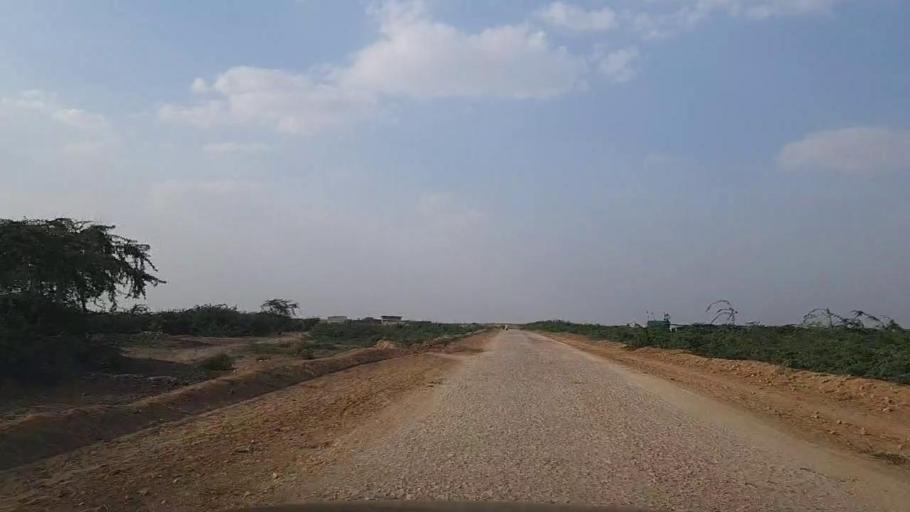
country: PK
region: Sindh
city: Gharo
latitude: 24.8026
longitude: 67.7426
